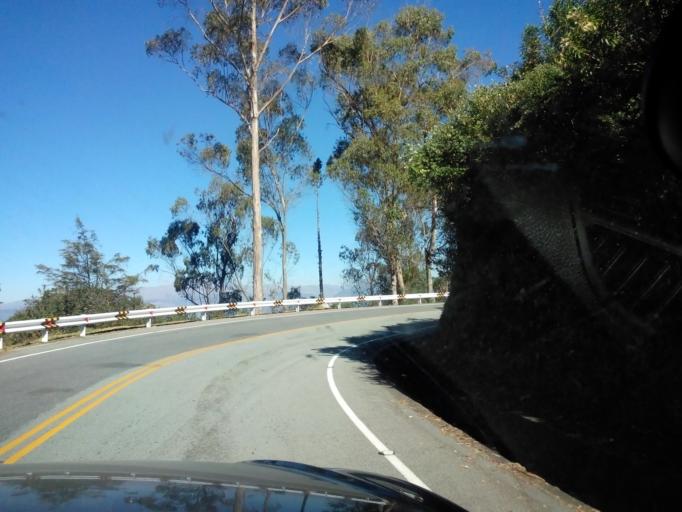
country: PE
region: Apurimac
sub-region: Provincia de Abancay
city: Tamburco
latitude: -13.5969
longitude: -72.8378
